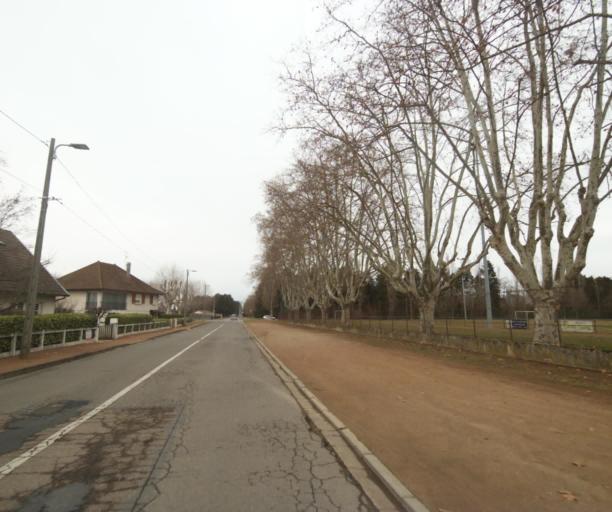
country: FR
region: Rhone-Alpes
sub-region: Departement de la Loire
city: Mably
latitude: 46.0658
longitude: 4.0787
